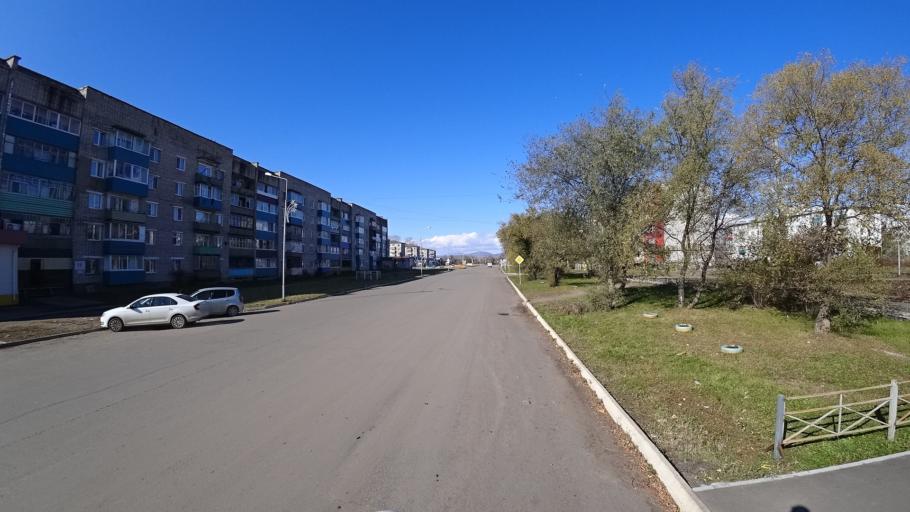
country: RU
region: Khabarovsk Krai
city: Amursk
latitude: 50.0995
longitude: 136.5154
